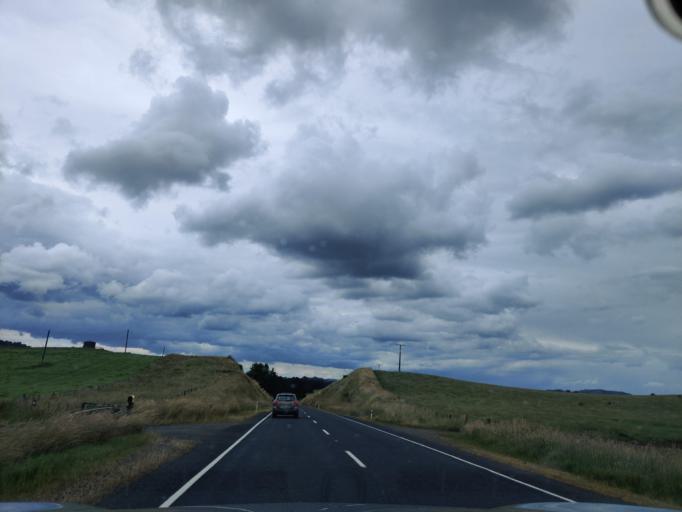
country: NZ
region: Manawatu-Wanganui
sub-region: Ruapehu District
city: Waiouru
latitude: -39.3922
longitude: 175.3698
